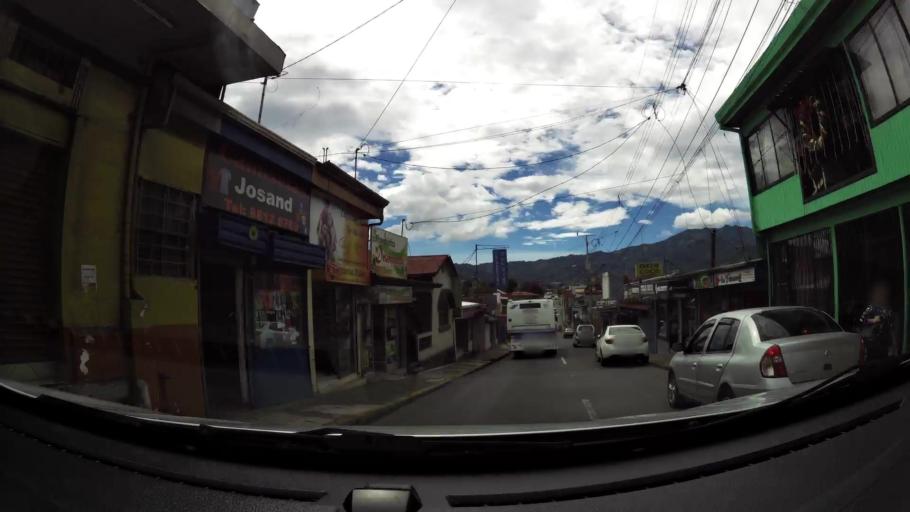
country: CR
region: San Jose
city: San Rafael Arriba
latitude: 9.8971
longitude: -84.0646
